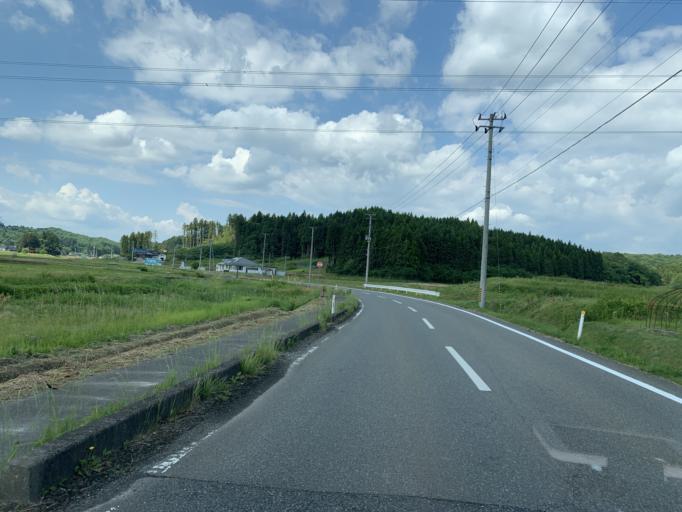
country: JP
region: Iwate
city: Ichinoseki
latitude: 38.7908
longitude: 140.9662
